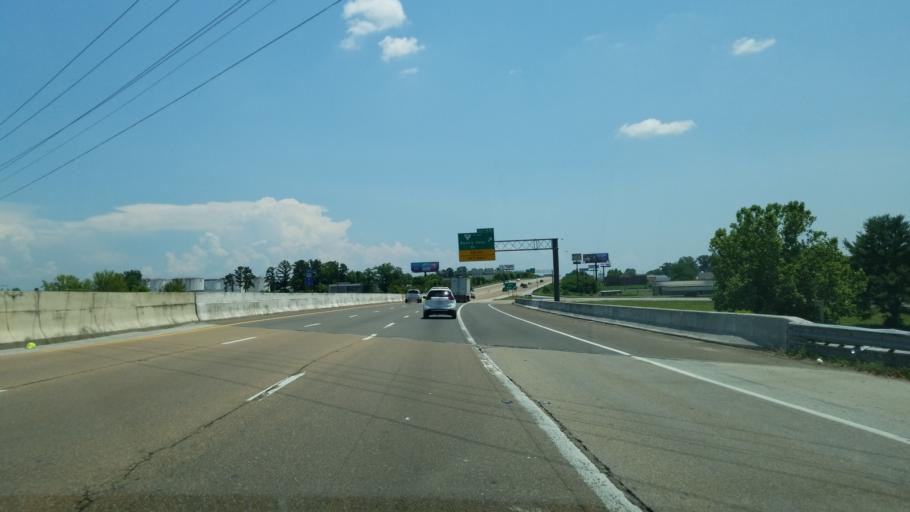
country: US
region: Tennessee
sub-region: Hamilton County
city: East Chattanooga
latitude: 35.0757
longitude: -85.1997
